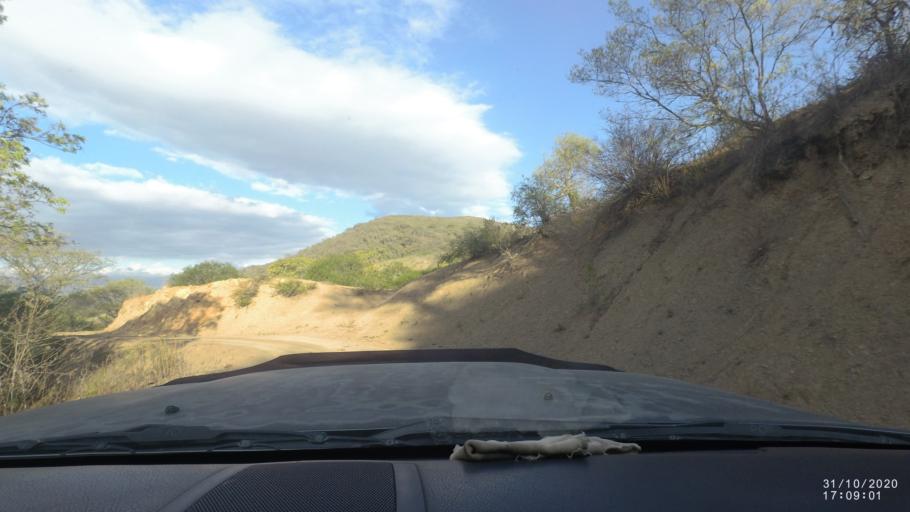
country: BO
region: Chuquisaca
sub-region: Provincia Zudanez
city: Mojocoya
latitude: -18.5485
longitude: -64.5391
